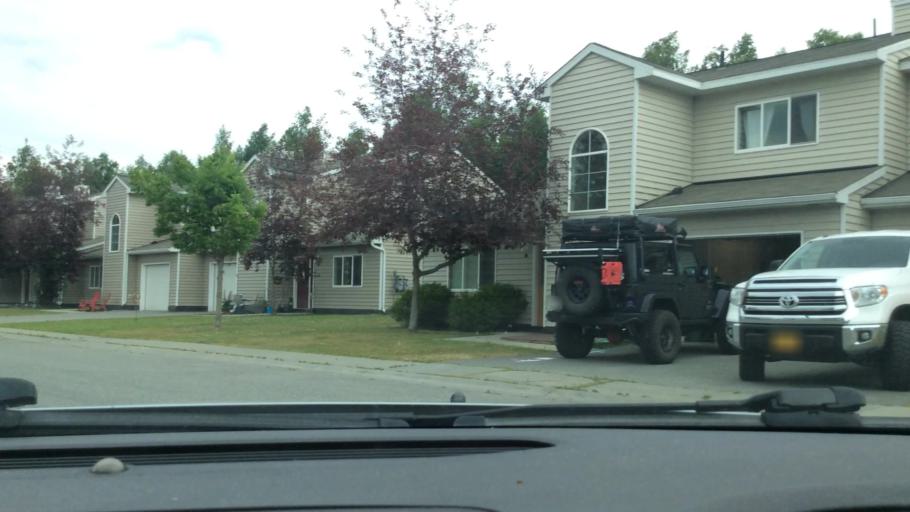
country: US
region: Alaska
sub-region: Anchorage Municipality
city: Anchorage
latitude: 61.2343
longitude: -149.7711
